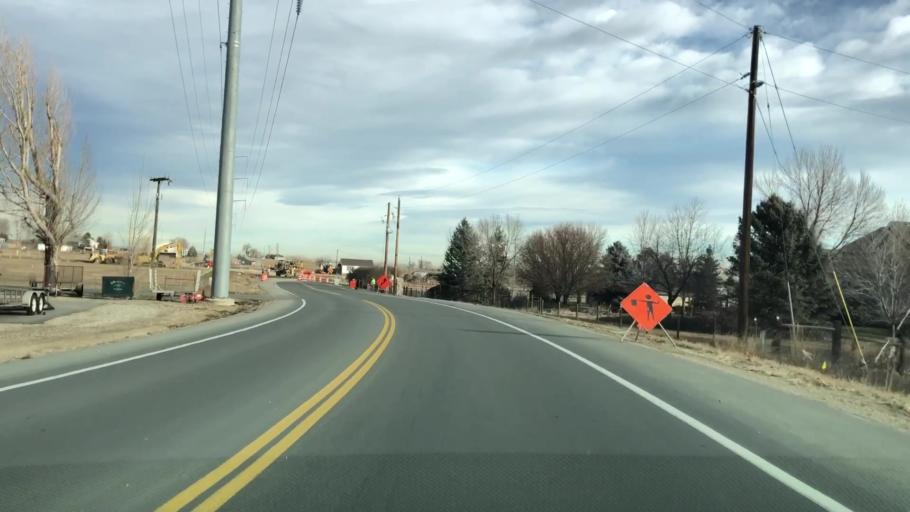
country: US
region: Colorado
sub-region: Larimer County
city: Loveland
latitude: 40.4489
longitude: -105.0444
